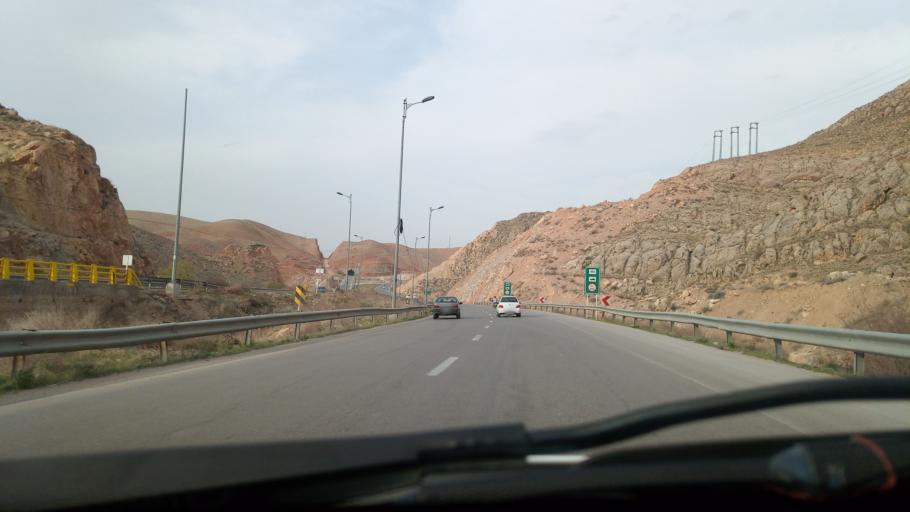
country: IR
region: Khorasan-e Shomali
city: Bojnurd
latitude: 37.4903
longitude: 57.4404
